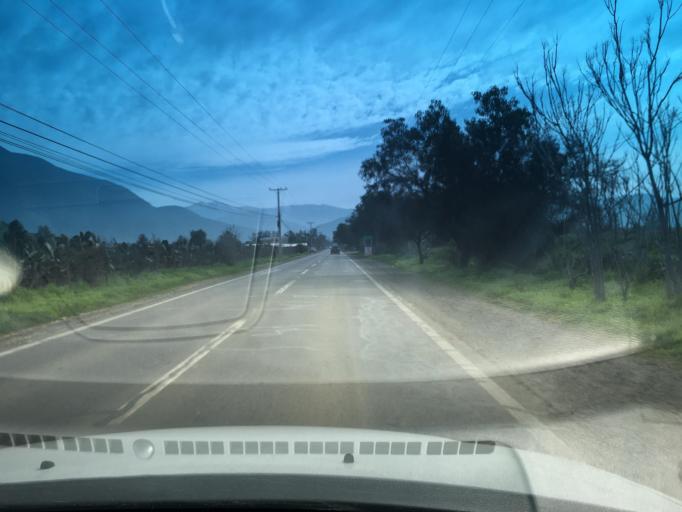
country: CL
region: Santiago Metropolitan
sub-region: Provincia de Chacabuco
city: Lampa
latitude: -33.0987
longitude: -70.9295
